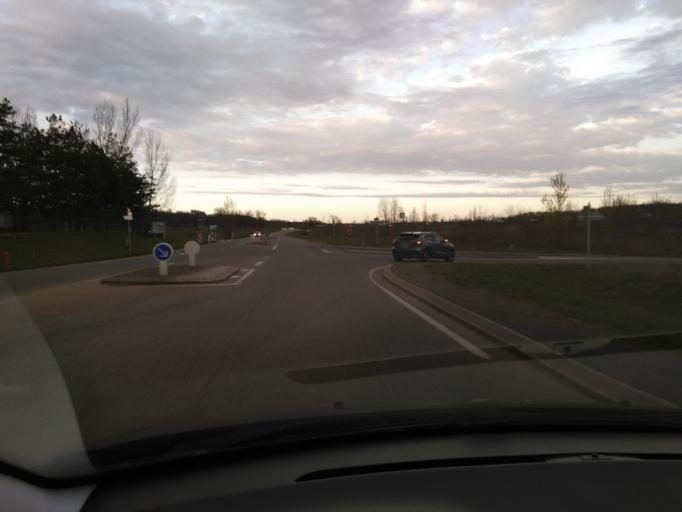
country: FR
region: Midi-Pyrenees
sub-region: Departement de la Haute-Garonne
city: La Salvetat-Saint-Gilles
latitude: 43.5959
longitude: 1.2766
